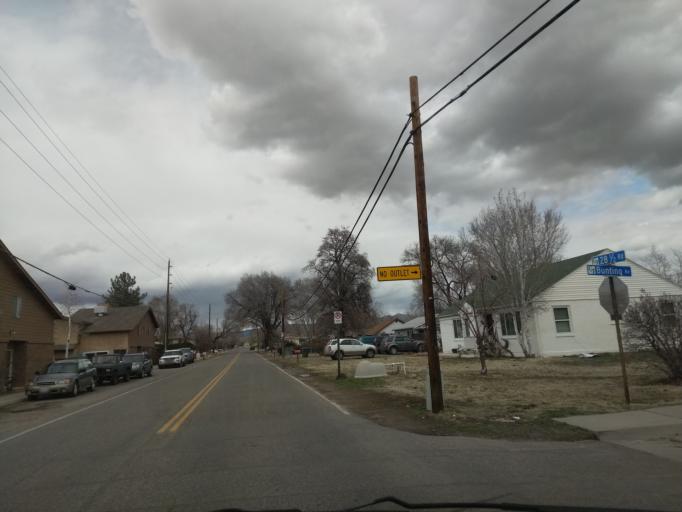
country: US
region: Colorado
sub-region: Mesa County
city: Fruitvale
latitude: 39.0795
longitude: -108.5245
